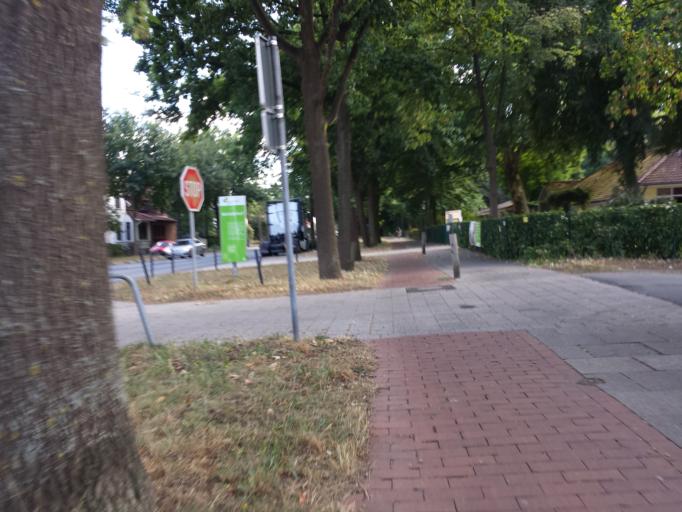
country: DE
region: Bremen
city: Bremen
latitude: 53.0423
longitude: 8.8153
